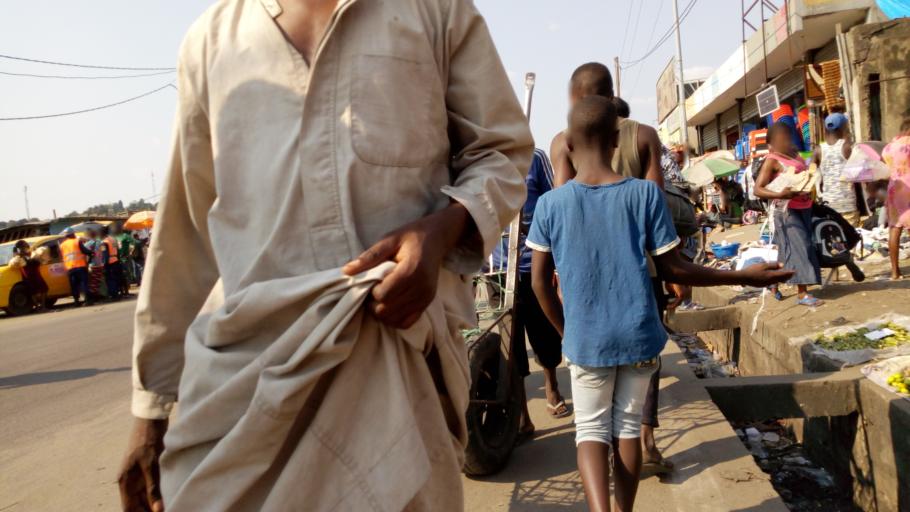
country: CD
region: Kinshasa
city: Kinshasa
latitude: -4.4495
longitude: 15.2480
